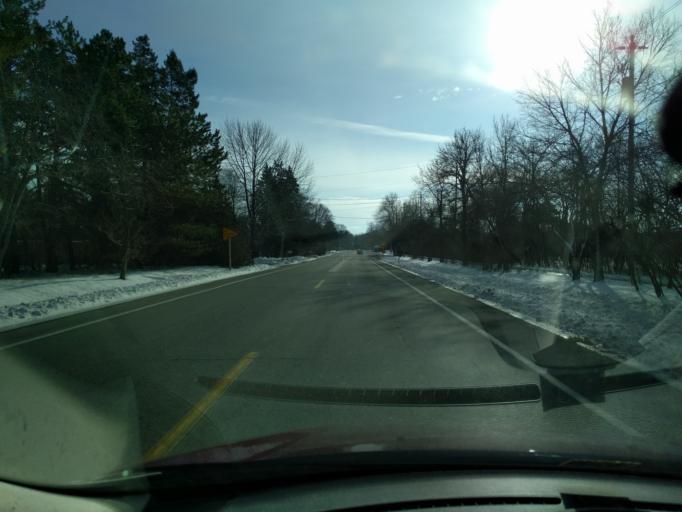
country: US
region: Wisconsin
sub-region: Milwaukee County
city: Fox Point
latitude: 43.1458
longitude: -87.9008
